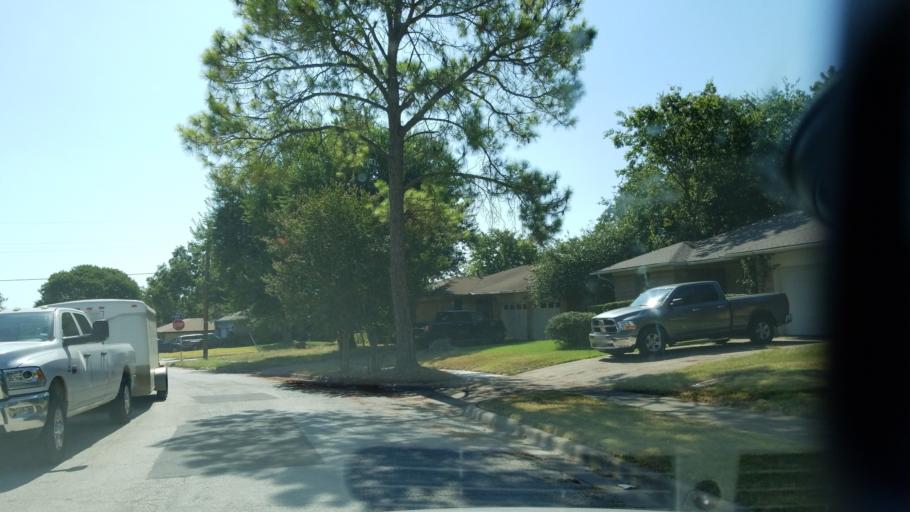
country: US
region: Texas
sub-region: Dallas County
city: Duncanville
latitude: 32.6455
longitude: -96.9017
